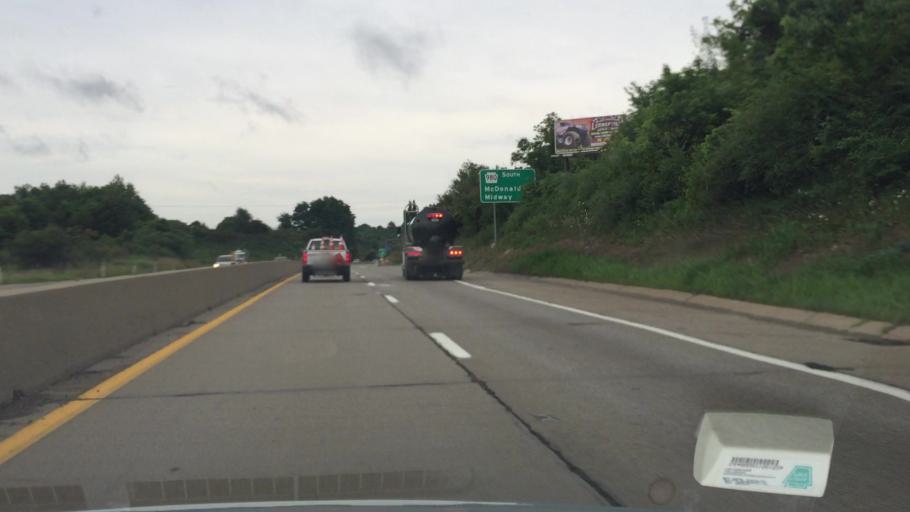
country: US
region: Pennsylvania
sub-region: Allegheny County
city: Imperial
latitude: 40.4252
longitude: -80.2987
